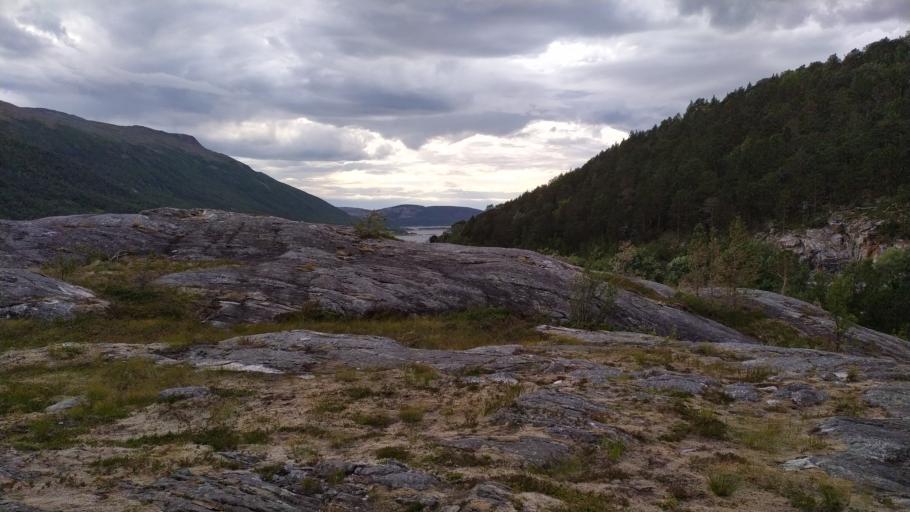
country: NO
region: Nordland
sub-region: Beiarn
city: Moldjord
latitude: 67.1799
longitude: 14.5999
